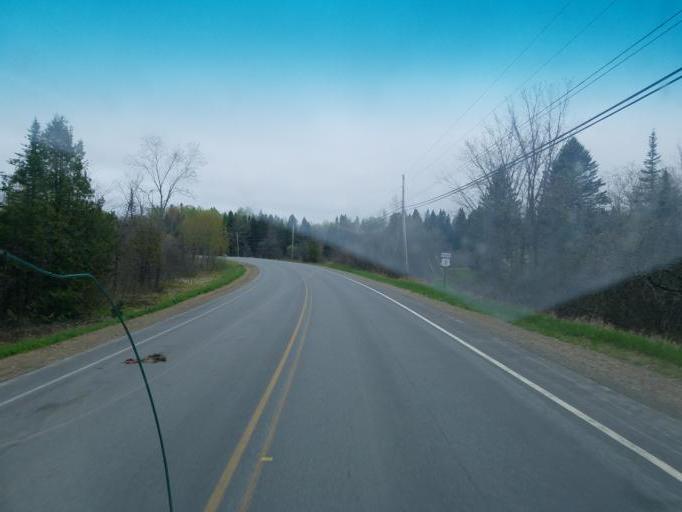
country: US
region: Maine
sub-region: Aroostook County
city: Hodgdon
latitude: 45.9945
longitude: -67.8631
